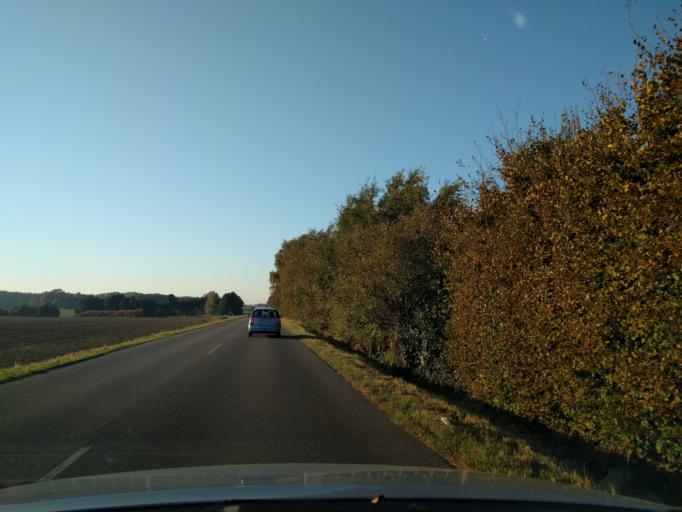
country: DK
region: Zealand
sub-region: Guldborgsund Kommune
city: Nykobing Falster
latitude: 54.7419
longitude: 11.9525
